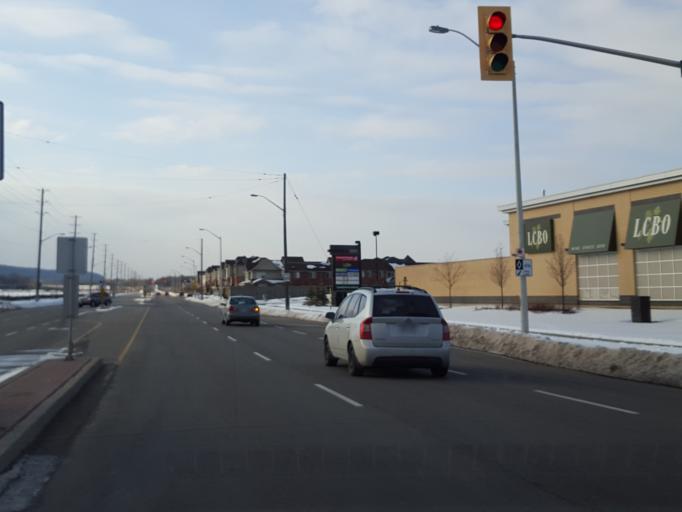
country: CA
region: Ontario
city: Burlington
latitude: 43.3923
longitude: -79.8240
